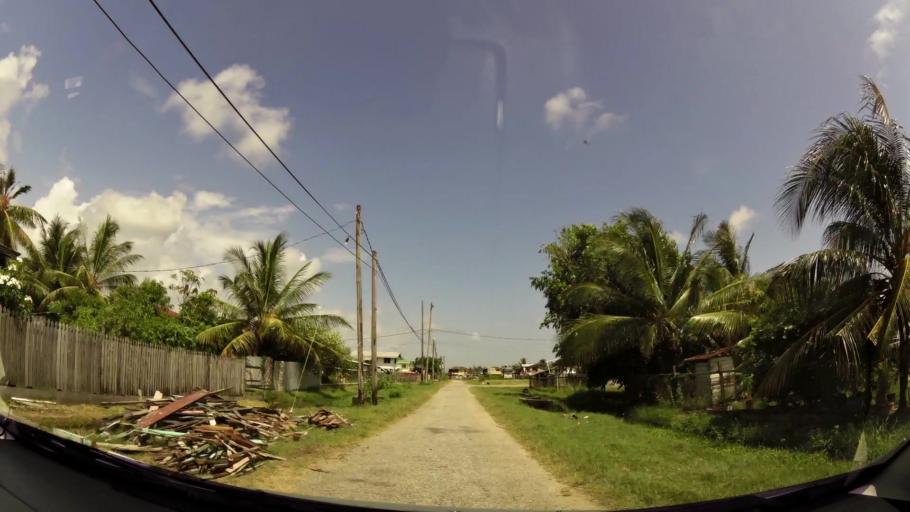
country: GY
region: Demerara-Mahaica
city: Mahaica Village
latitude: 6.7694
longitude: -58.0089
